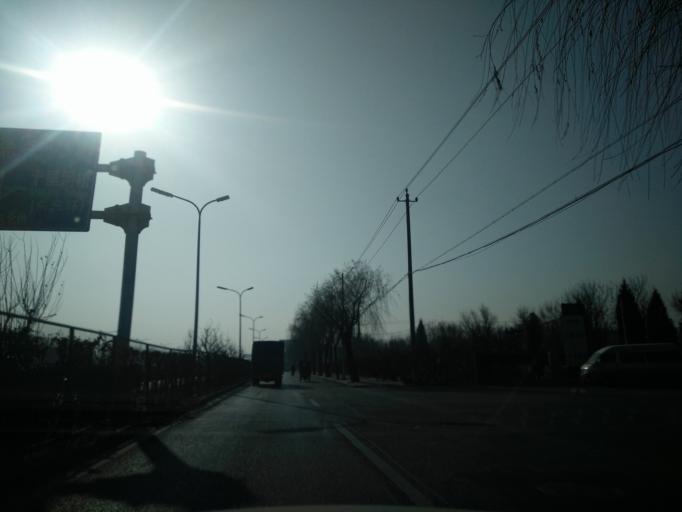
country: CN
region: Beijing
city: Jiugong
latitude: 39.8552
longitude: 116.4801
